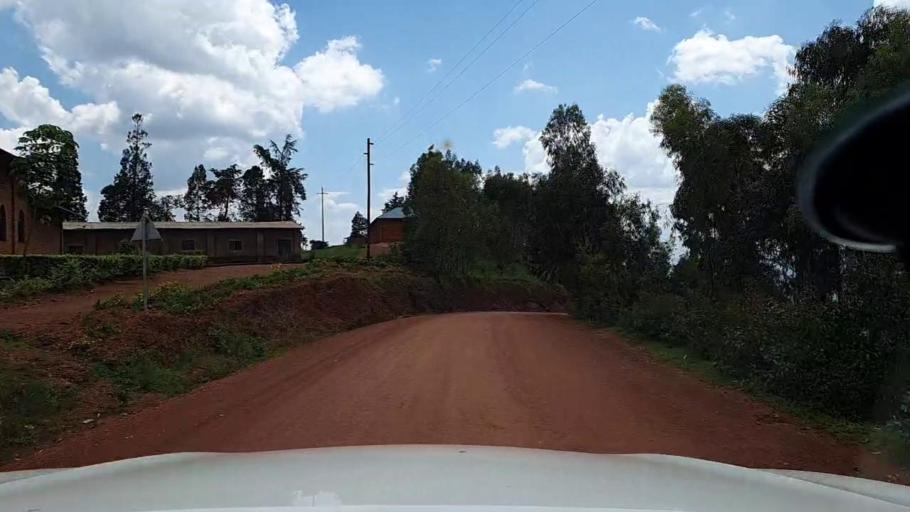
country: RW
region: Kigali
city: Kigali
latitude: -1.7983
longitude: 29.8439
